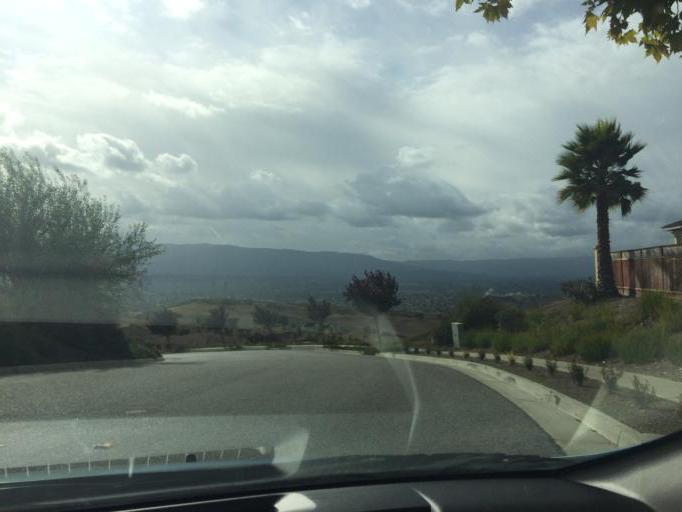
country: US
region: California
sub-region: Santa Clara County
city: Seven Trees
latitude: 37.2861
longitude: -121.7927
